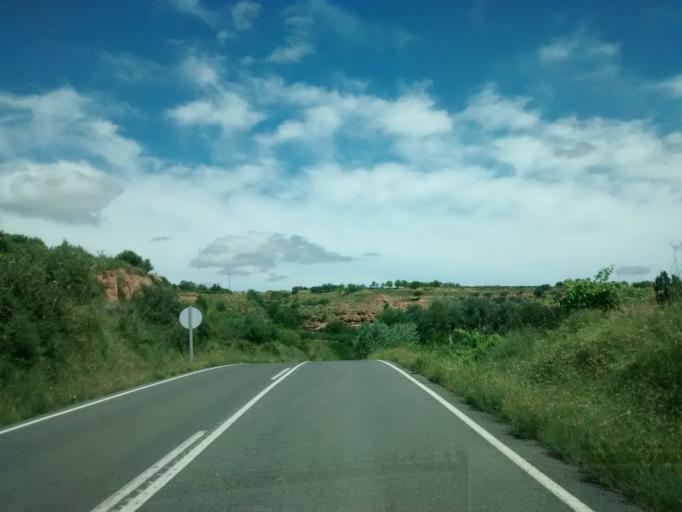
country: ES
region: La Rioja
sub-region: Provincia de La Rioja
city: Leza de Rio Leza
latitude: 42.3533
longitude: -2.3938
